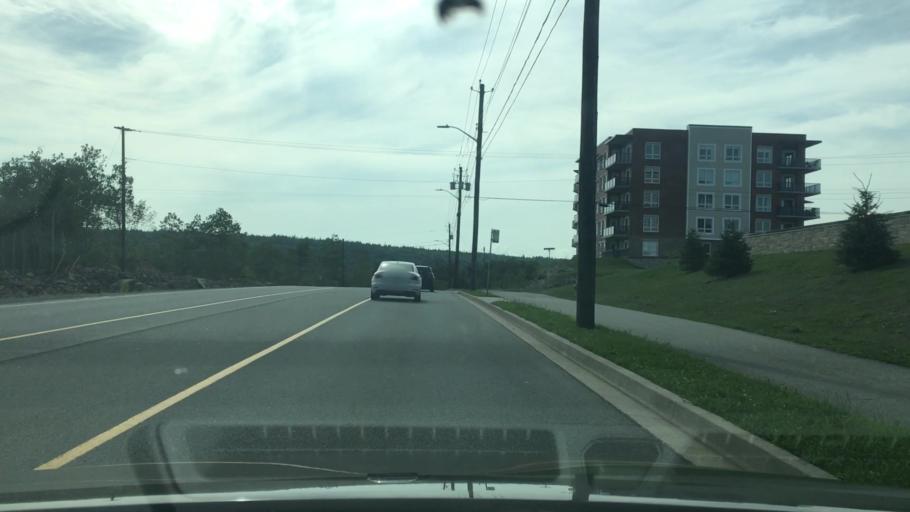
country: CA
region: Nova Scotia
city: Dartmouth
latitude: 44.6997
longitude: -63.6971
